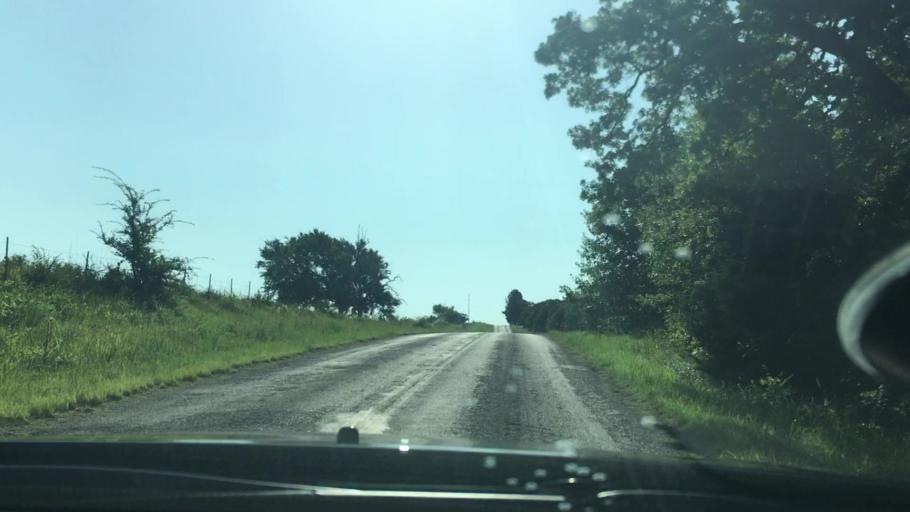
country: US
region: Oklahoma
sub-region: Pontotoc County
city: Ada
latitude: 34.8106
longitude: -96.6408
